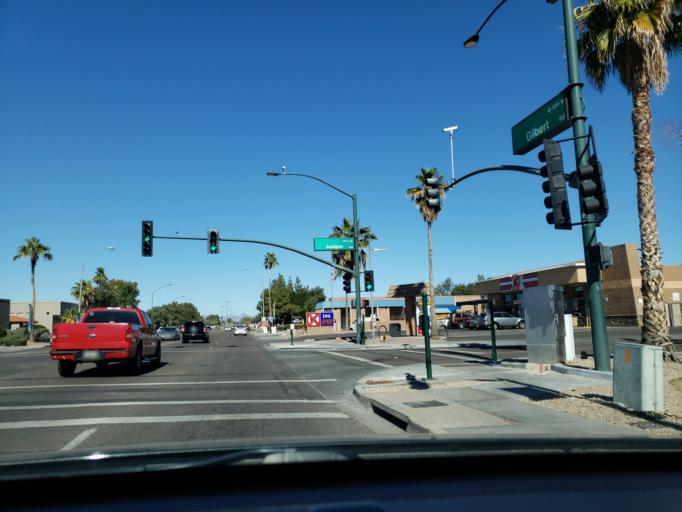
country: US
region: Arizona
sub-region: Maricopa County
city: Gilbert
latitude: 33.3594
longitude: -111.7897
